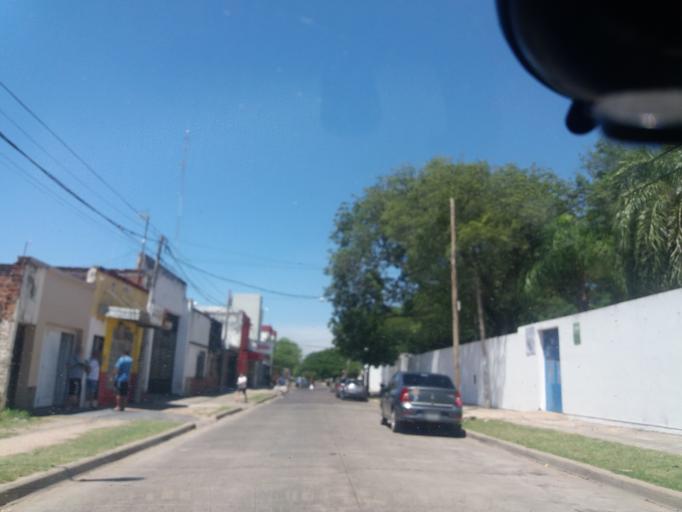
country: AR
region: Corrientes
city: Corrientes
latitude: -27.4835
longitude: -58.8455
